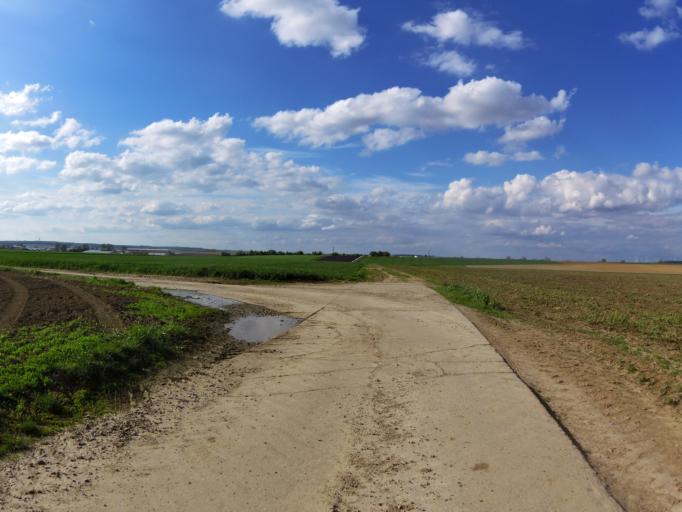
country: DE
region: Bavaria
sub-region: Regierungsbezirk Unterfranken
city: Oberpleichfeld
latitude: 49.8622
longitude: 10.0692
